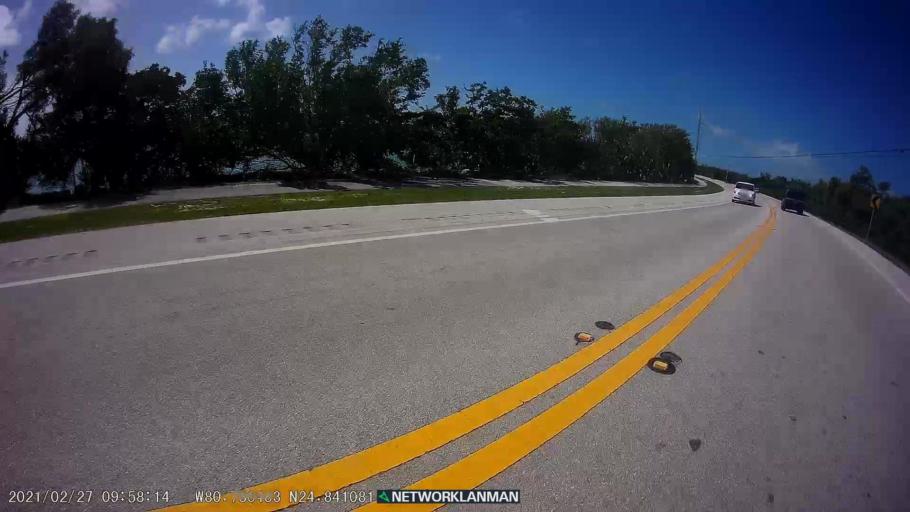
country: US
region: Florida
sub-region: Monroe County
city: Islamorada
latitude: 24.8408
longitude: -80.7866
